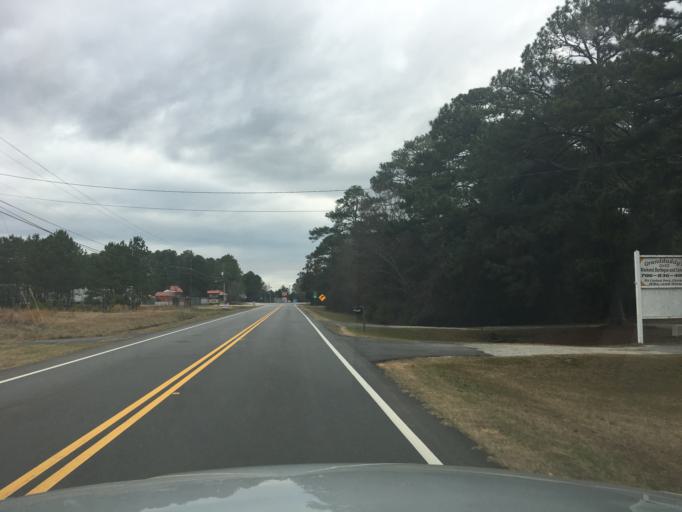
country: US
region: Georgia
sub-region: Columbia County
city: Appling
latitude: 33.6643
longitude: -82.3361
